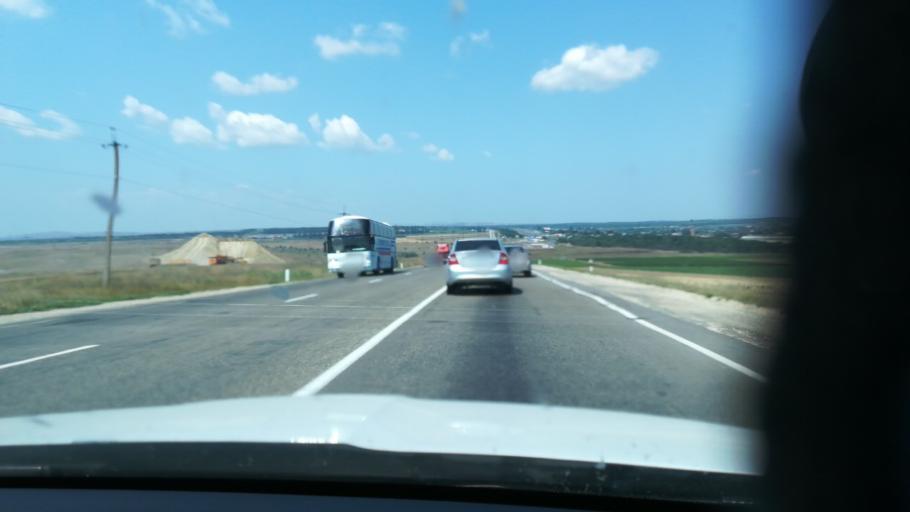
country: RU
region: Krasnodarskiy
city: Starotitarovskaya
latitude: 45.1899
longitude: 37.1780
